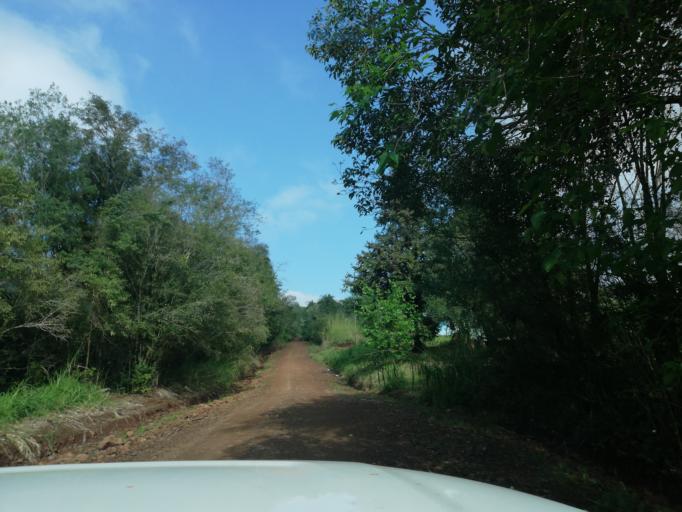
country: AR
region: Misiones
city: Cerro Azul
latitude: -27.5732
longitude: -55.5019
